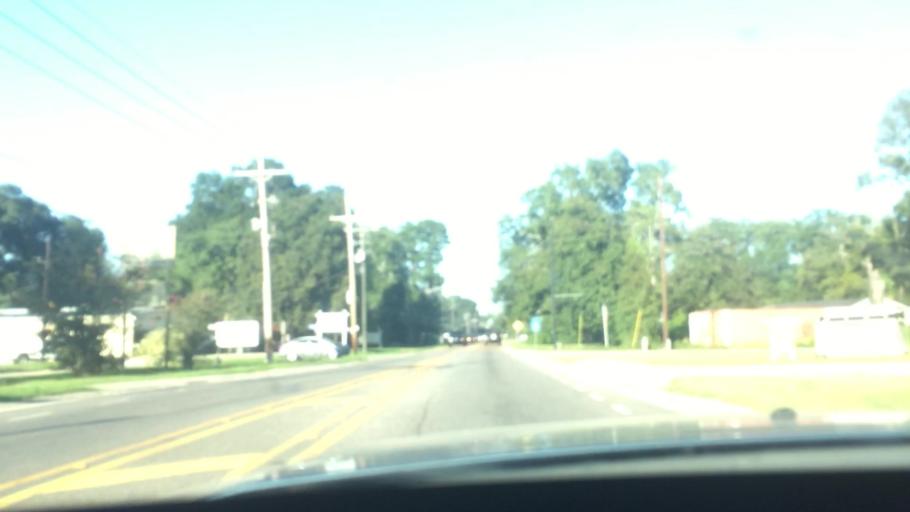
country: US
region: Louisiana
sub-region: East Baton Rouge Parish
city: Monticello
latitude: 30.4530
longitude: -91.0220
